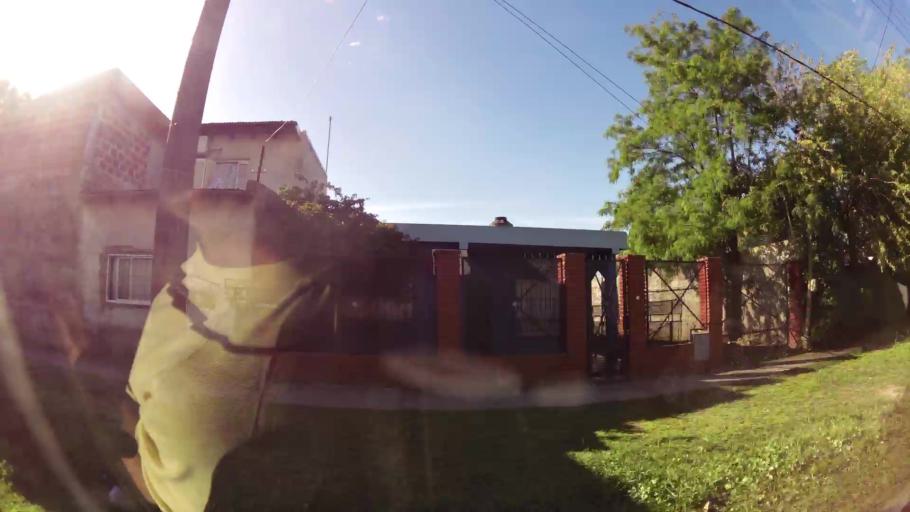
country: AR
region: Buenos Aires
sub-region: Partido de Almirante Brown
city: Adrogue
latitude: -34.8255
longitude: -58.3465
